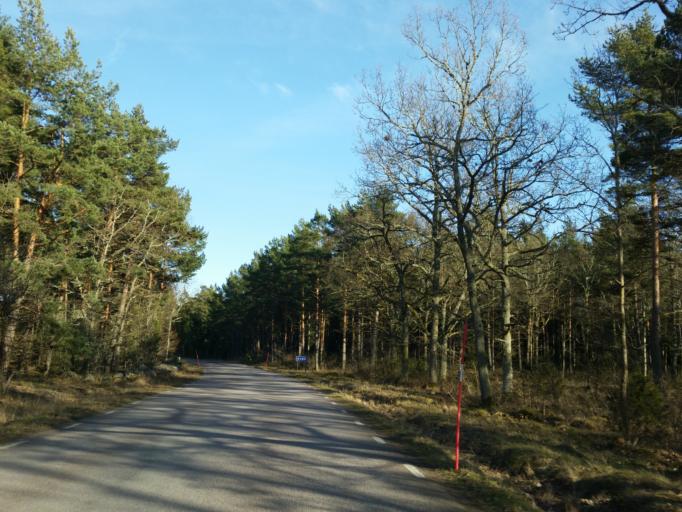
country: SE
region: Kalmar
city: Faerjestaden
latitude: 56.7826
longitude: 16.4354
